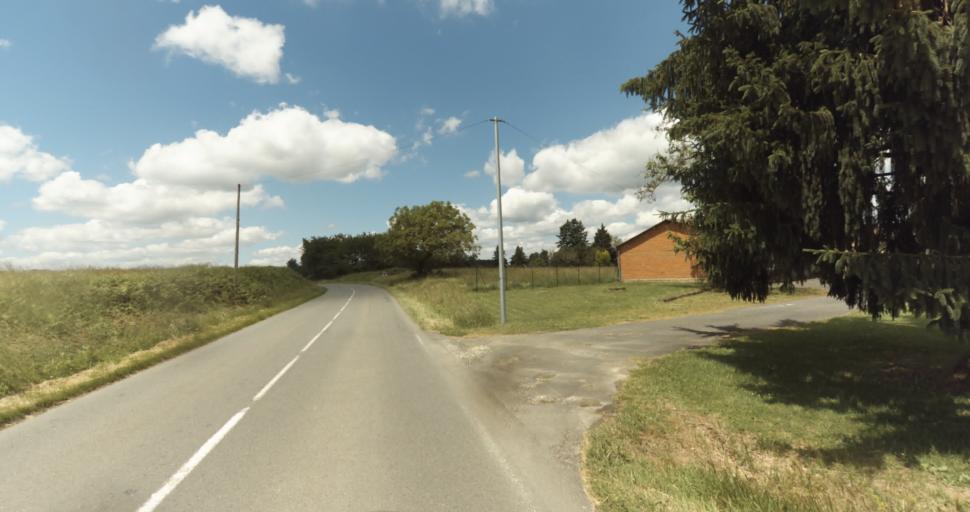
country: FR
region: Aquitaine
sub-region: Departement de la Dordogne
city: Beaumont-du-Perigord
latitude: 44.6898
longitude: 0.8832
